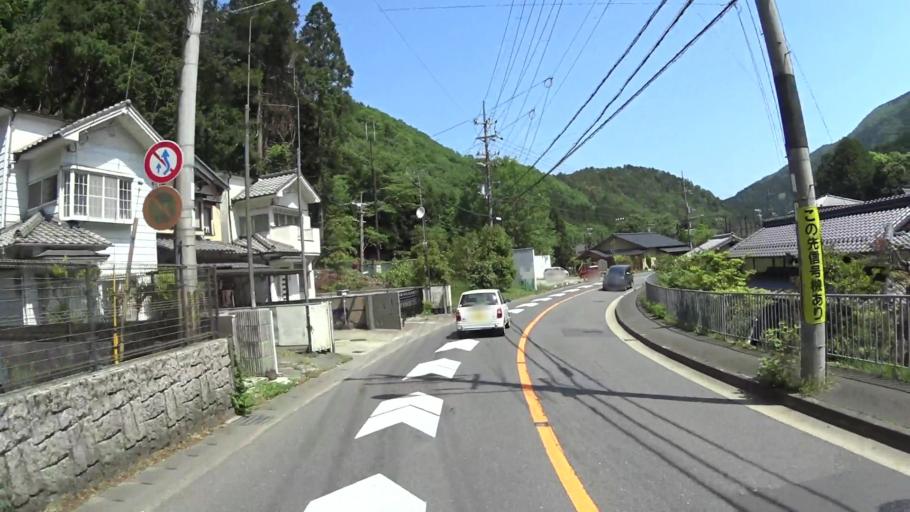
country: JP
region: Kyoto
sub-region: Kyoto-shi
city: Kamigyo-ku
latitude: 35.0825
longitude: 135.8171
